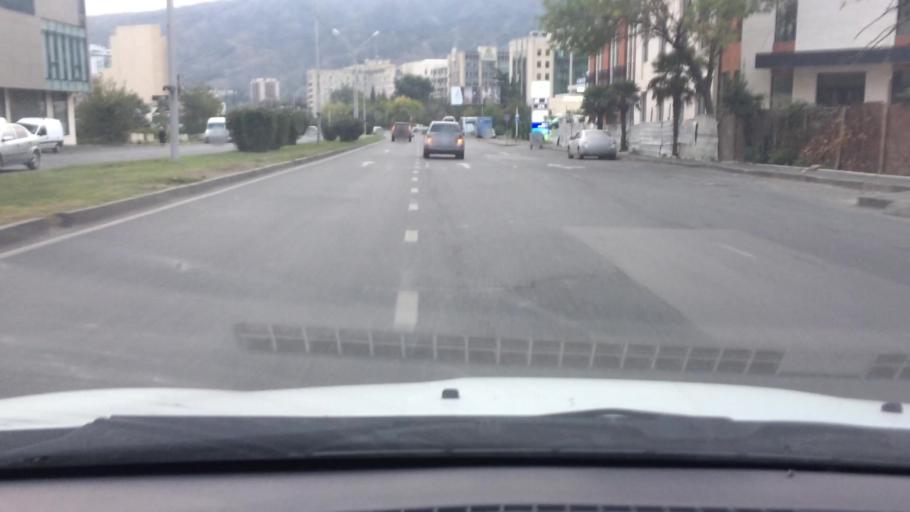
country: GE
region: T'bilisi
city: Tbilisi
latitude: 41.6816
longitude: 44.8264
